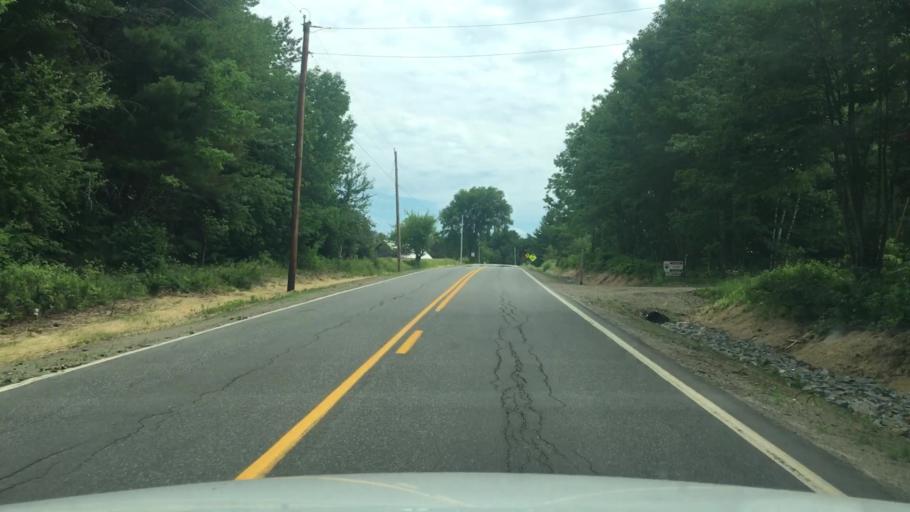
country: US
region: Maine
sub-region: Waldo County
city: Searsmont
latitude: 44.4571
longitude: -69.2658
